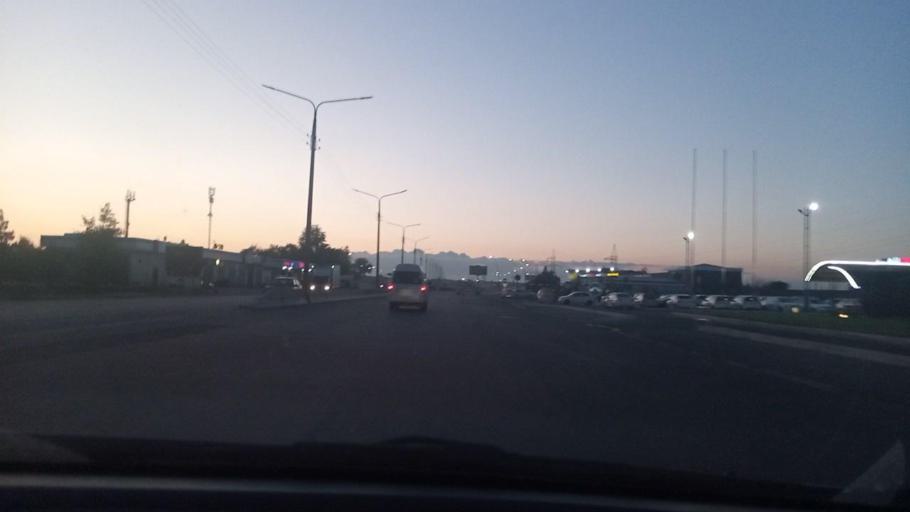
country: UZ
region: Toshkent Shahri
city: Tashkent
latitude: 41.2440
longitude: 69.2321
